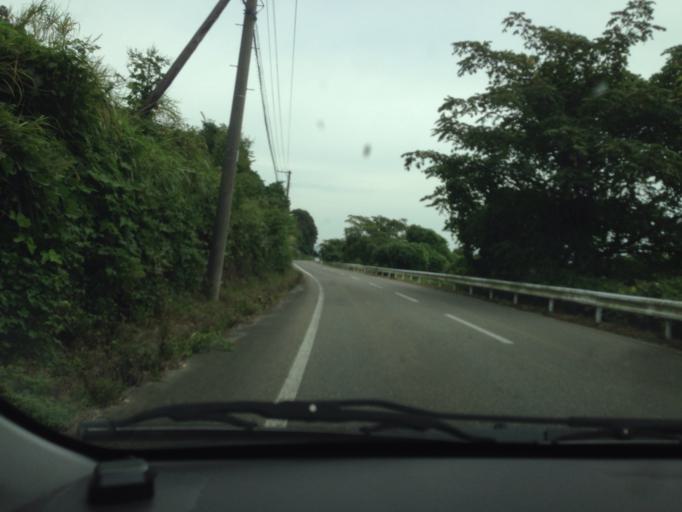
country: JP
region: Fukushima
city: Kitakata
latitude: 37.6126
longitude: 139.8106
